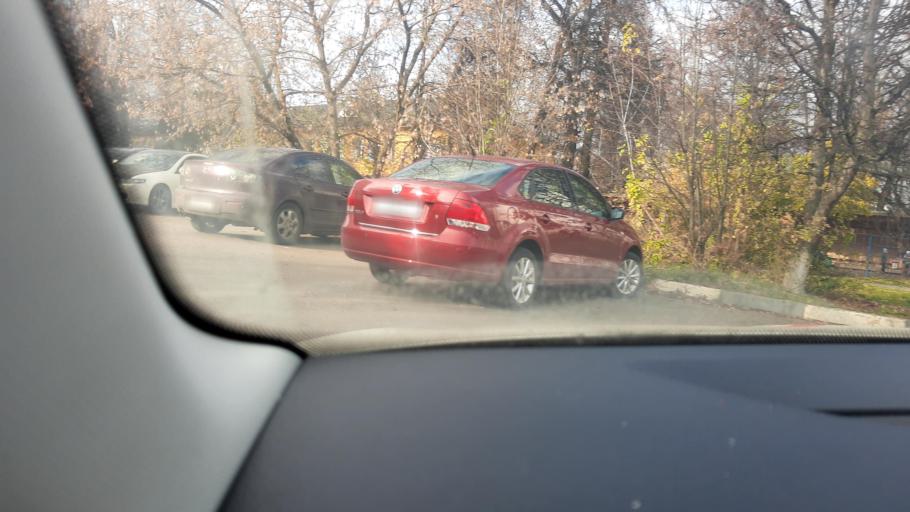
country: RU
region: Moskovskaya
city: Shcherbinka
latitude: 55.4722
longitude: 37.6126
